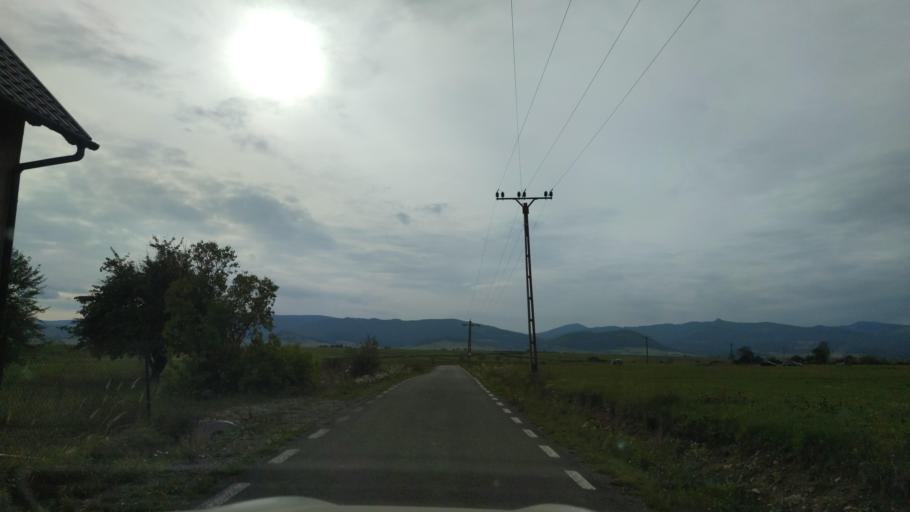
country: RO
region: Harghita
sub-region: Comuna Remetea
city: Remetea
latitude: 46.8080
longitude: 25.4352
